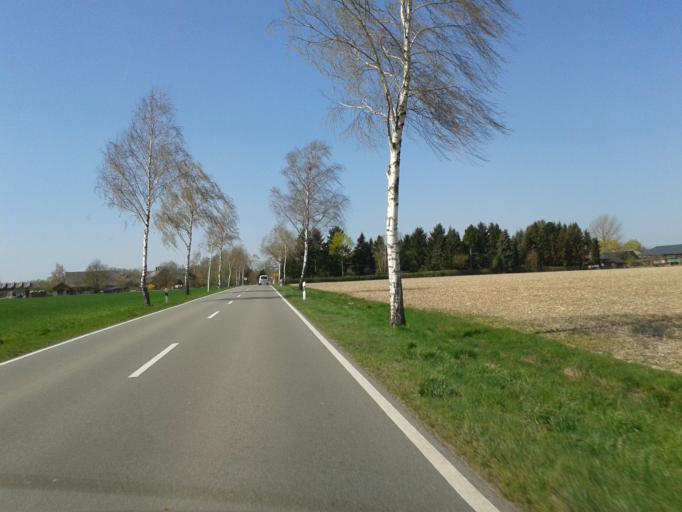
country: DE
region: Lower Saxony
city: Wustrow
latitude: 52.9385
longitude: 11.1034
